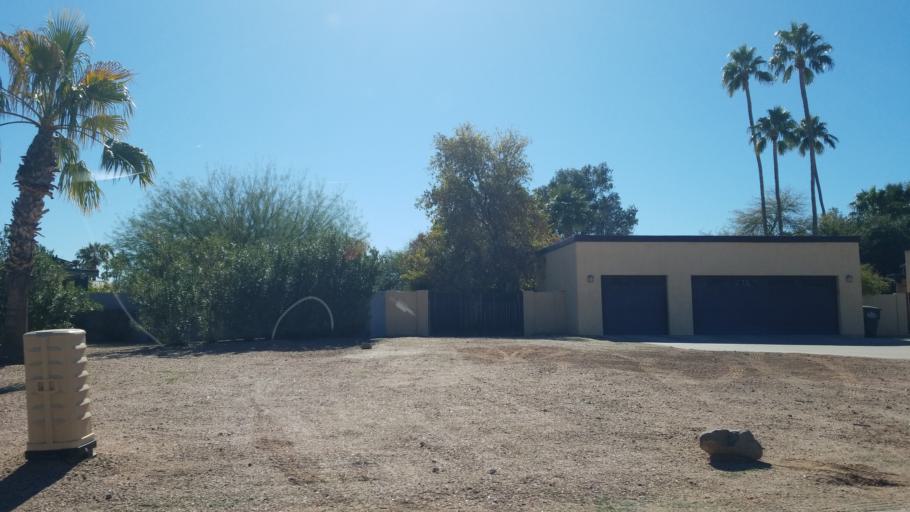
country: US
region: Arizona
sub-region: Maricopa County
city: Paradise Valley
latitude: 33.6150
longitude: -111.9394
